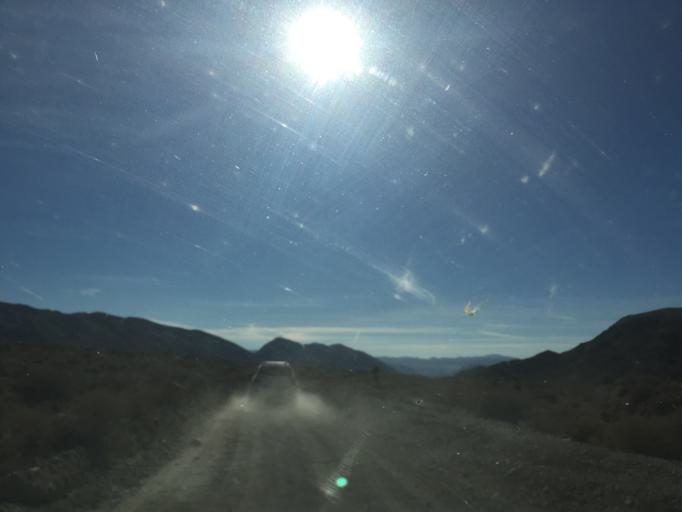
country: US
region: California
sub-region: Inyo County
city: Lone Pine
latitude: 36.8116
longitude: -117.5103
